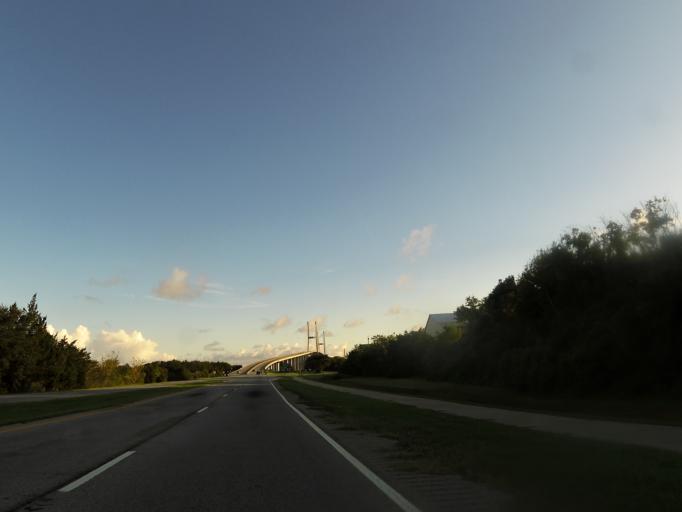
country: US
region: Georgia
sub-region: Glynn County
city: Brunswick
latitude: 31.1303
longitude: -81.4796
